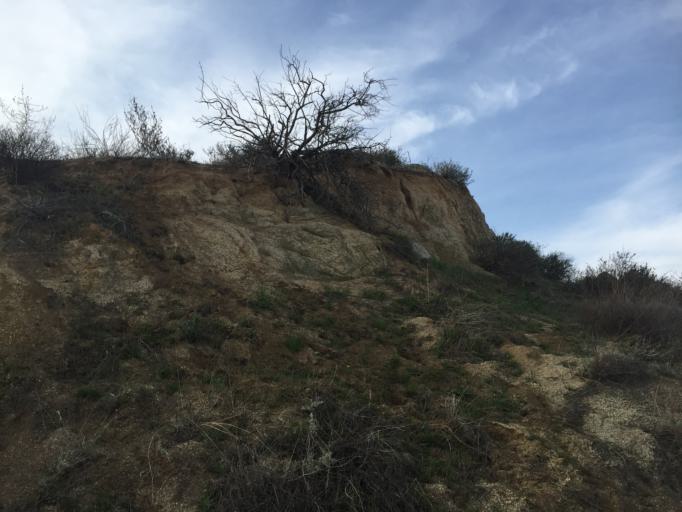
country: US
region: California
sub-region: San Bernardino County
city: Grand Terrace
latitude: 34.0279
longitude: -117.2966
